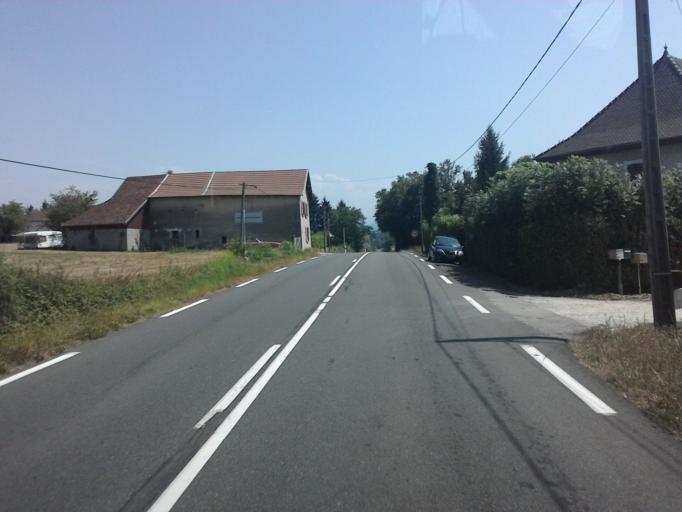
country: FR
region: Rhone-Alpes
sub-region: Departement de l'Isere
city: La Batie-Montgascon
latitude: 45.5801
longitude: 5.5509
